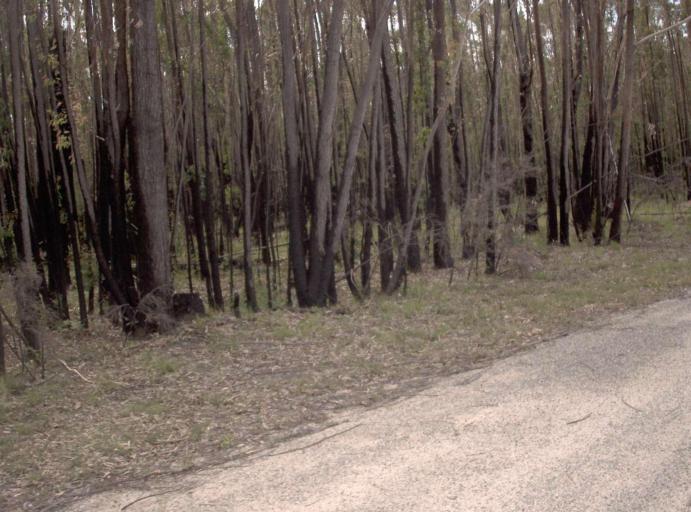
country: AU
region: New South Wales
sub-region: Bega Valley
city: Eden
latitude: -37.5252
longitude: 149.4904
